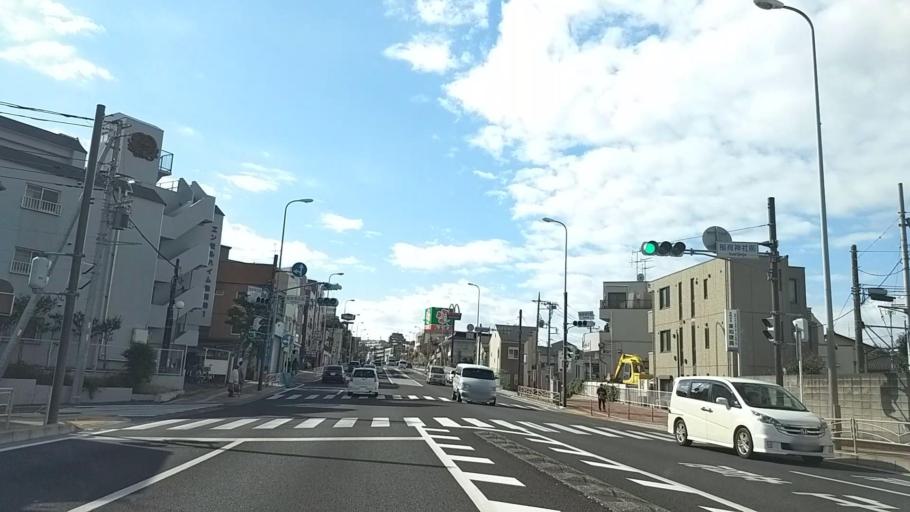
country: JP
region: Kanagawa
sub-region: Kawasaki-shi
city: Kawasaki
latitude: 35.5173
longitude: 139.6676
